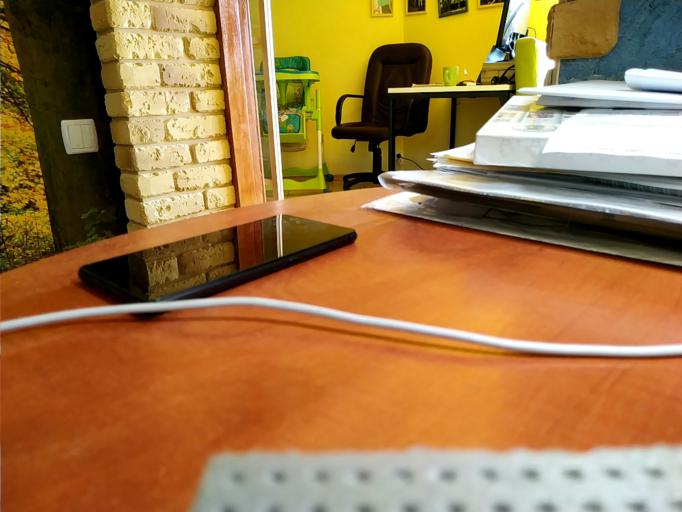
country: RU
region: Tverskaya
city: Kalashnikovo
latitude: 57.3833
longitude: 35.3356
